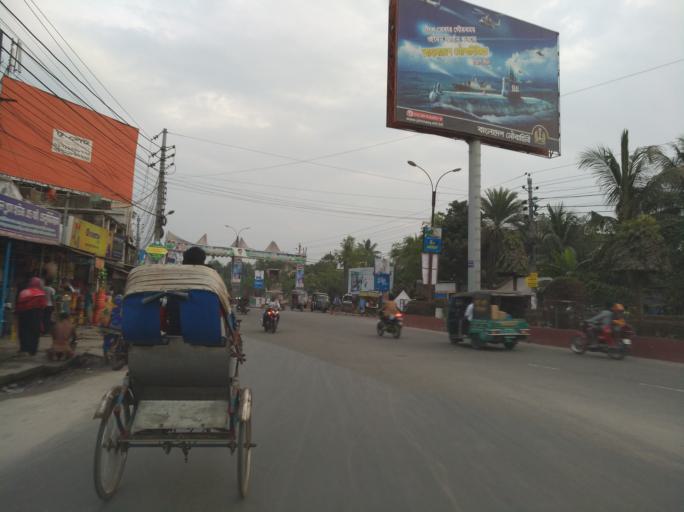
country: BD
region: Khulna
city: Khulna
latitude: 22.8286
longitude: 89.5499
